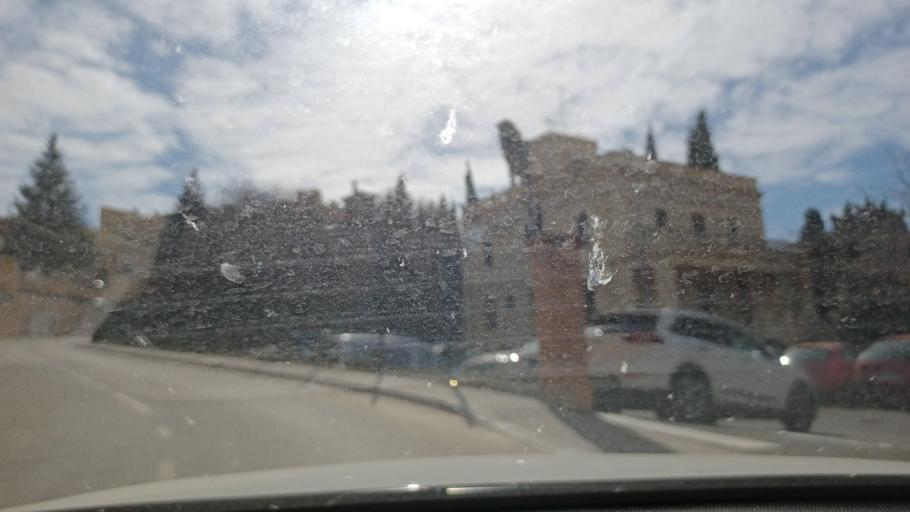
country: ES
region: Catalonia
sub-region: Provincia de Barcelona
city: Gelida
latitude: 41.4423
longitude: 1.8633
